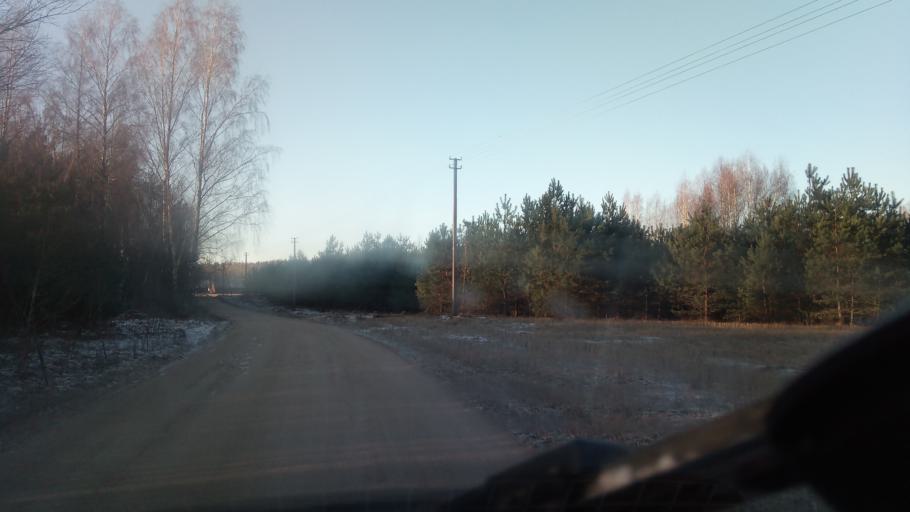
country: LT
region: Alytaus apskritis
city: Druskininkai
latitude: 54.1607
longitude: 23.9570
